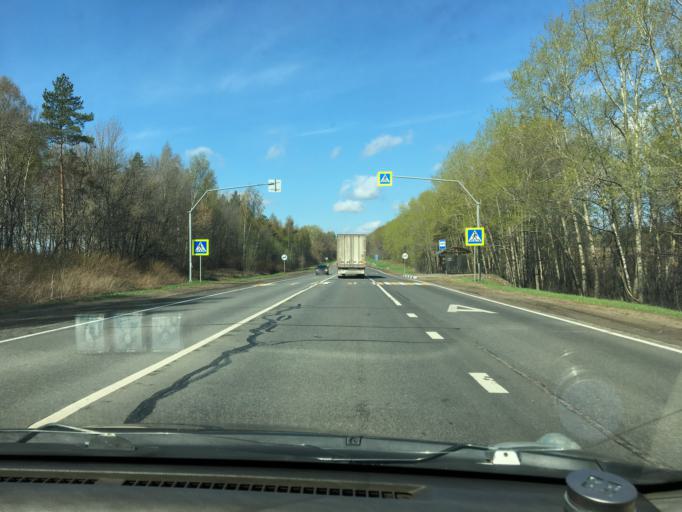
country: RU
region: Nizjnij Novgorod
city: Pamyat' Parizhskoy Kommuny
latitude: 56.0281
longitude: 44.5616
